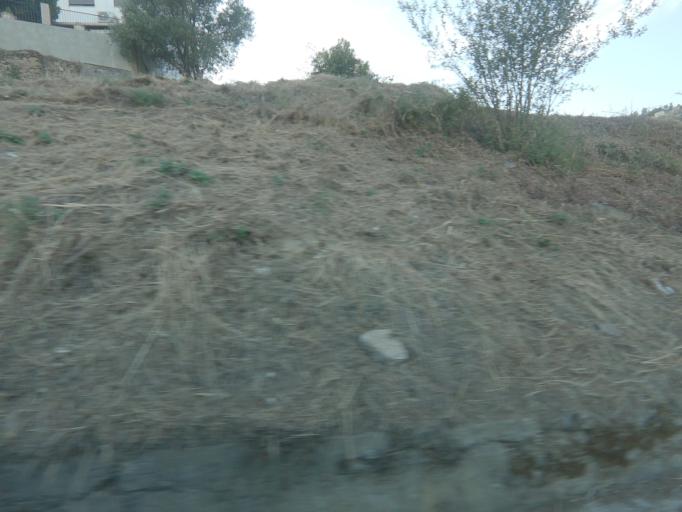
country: PT
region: Vila Real
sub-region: Peso da Regua
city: Godim
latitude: 41.1650
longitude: -7.8098
